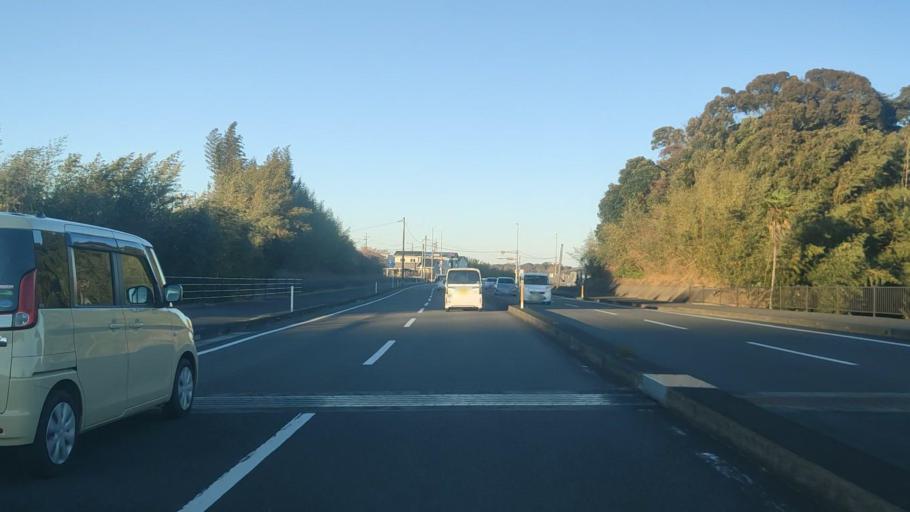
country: JP
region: Miyazaki
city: Miyazaki-shi
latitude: 31.8881
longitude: 131.4026
